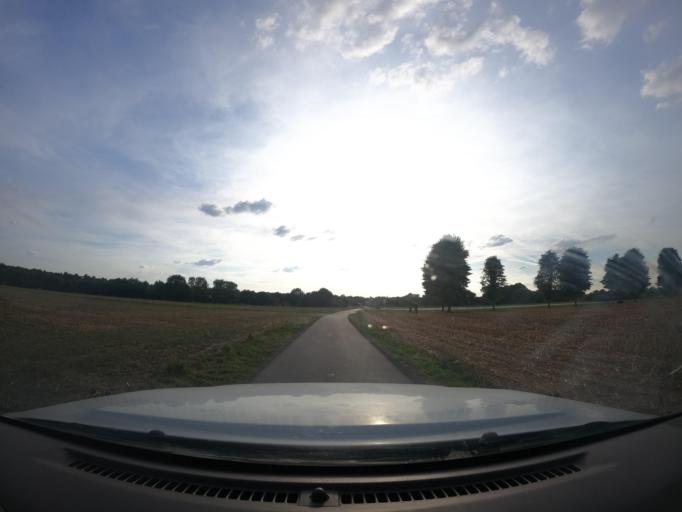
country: DE
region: North Rhine-Westphalia
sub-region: Regierungsbezirk Dusseldorf
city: Hamminkeln
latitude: 51.7009
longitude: 6.5876
